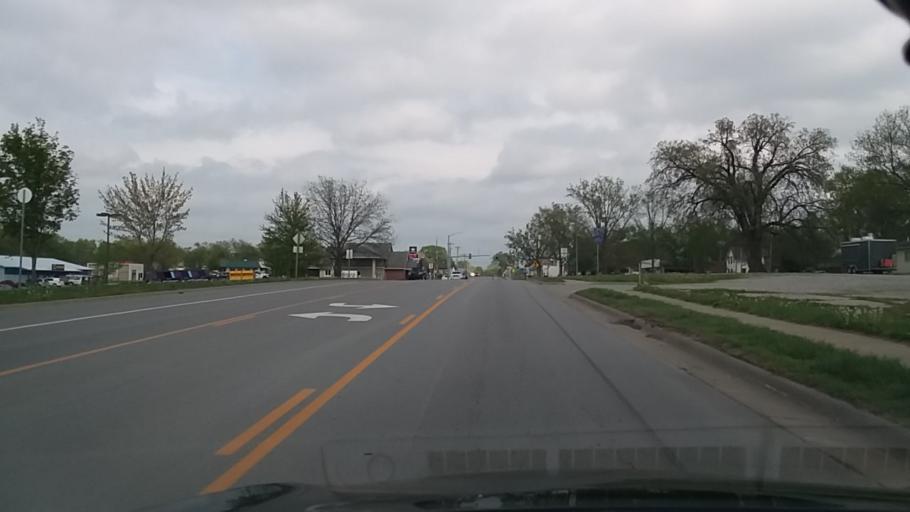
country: US
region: Kansas
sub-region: Douglas County
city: Baldwin City
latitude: 38.7822
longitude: -95.1887
